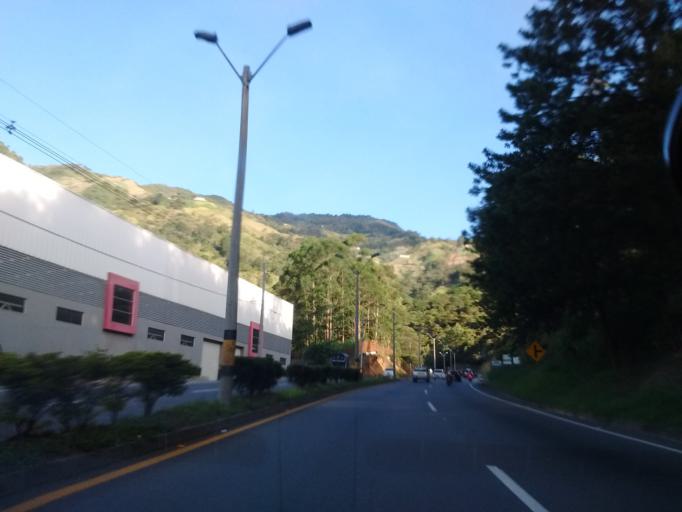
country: CO
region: Antioquia
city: Bello
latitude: 6.3196
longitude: -75.5325
